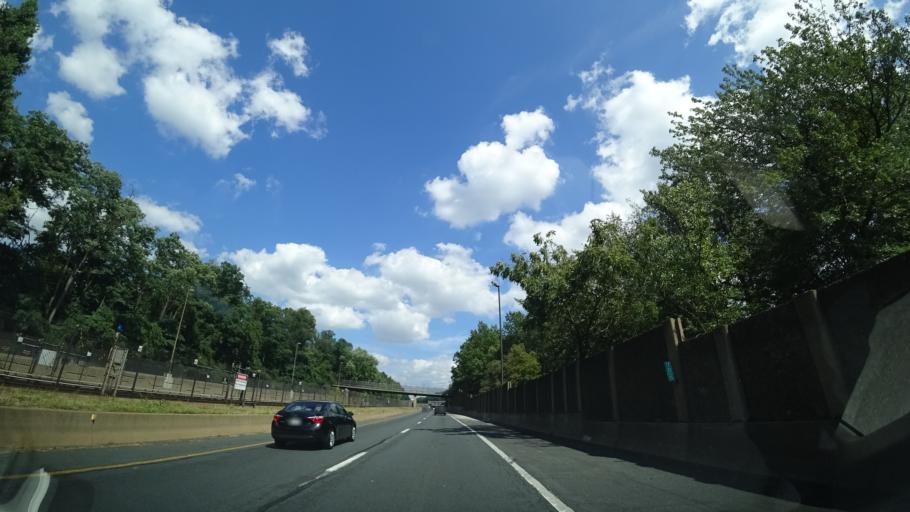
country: US
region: Virginia
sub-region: Fairfax County
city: Seven Corners
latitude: 38.8791
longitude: -77.1354
